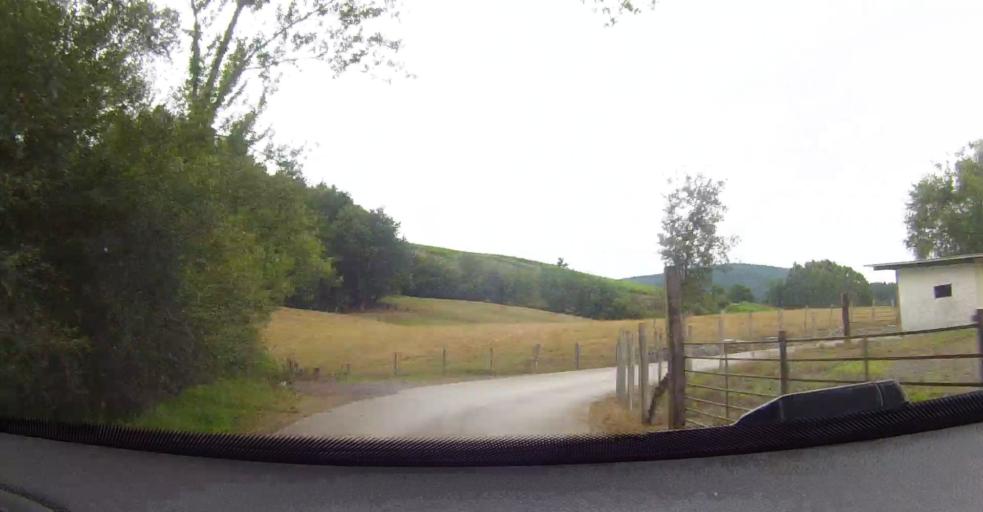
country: ES
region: Basque Country
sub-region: Bizkaia
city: Urrestieta
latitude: 43.2291
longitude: -3.1662
